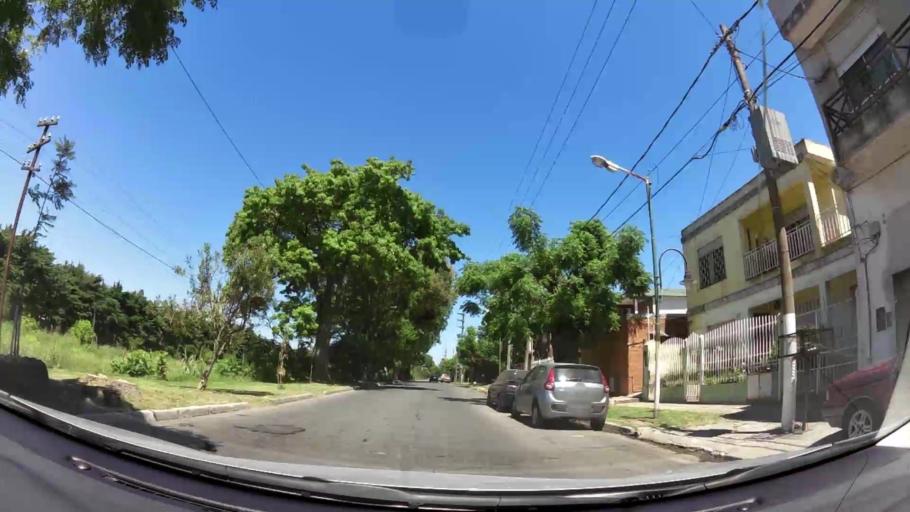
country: AR
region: Buenos Aires
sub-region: Partido de Tigre
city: Tigre
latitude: -34.4634
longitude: -58.5570
